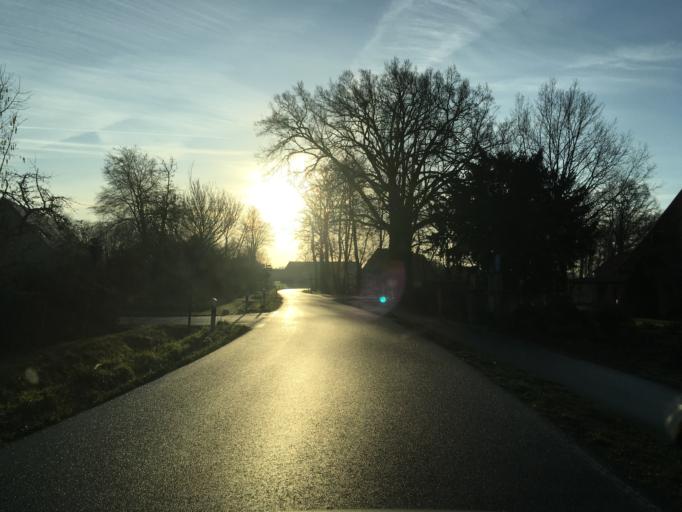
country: DE
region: North Rhine-Westphalia
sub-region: Regierungsbezirk Munster
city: Schoppingen
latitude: 52.0757
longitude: 7.2577
